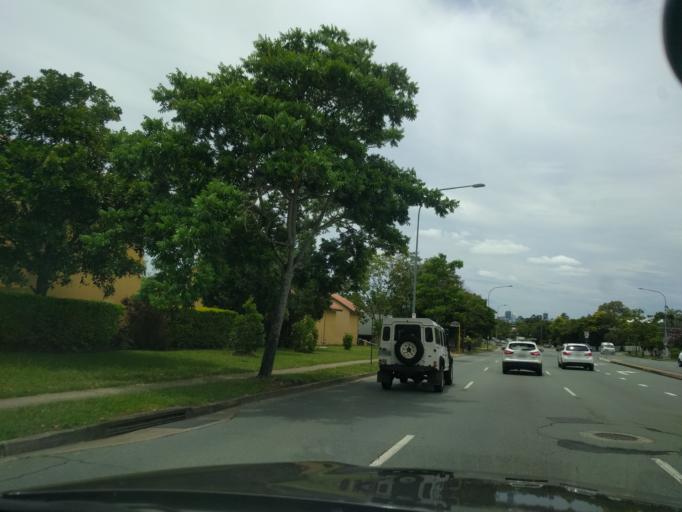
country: AU
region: Queensland
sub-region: Brisbane
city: Grange
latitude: -27.4265
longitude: 153.0020
